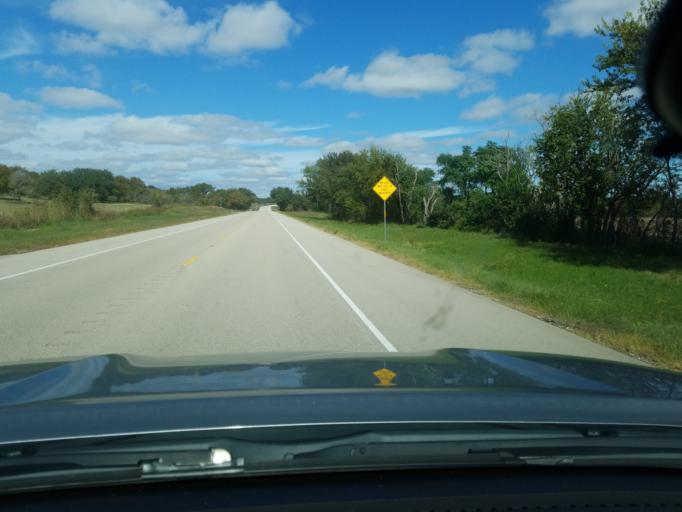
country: US
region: Texas
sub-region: Hamilton County
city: Hamilton
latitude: 31.6056
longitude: -98.1582
